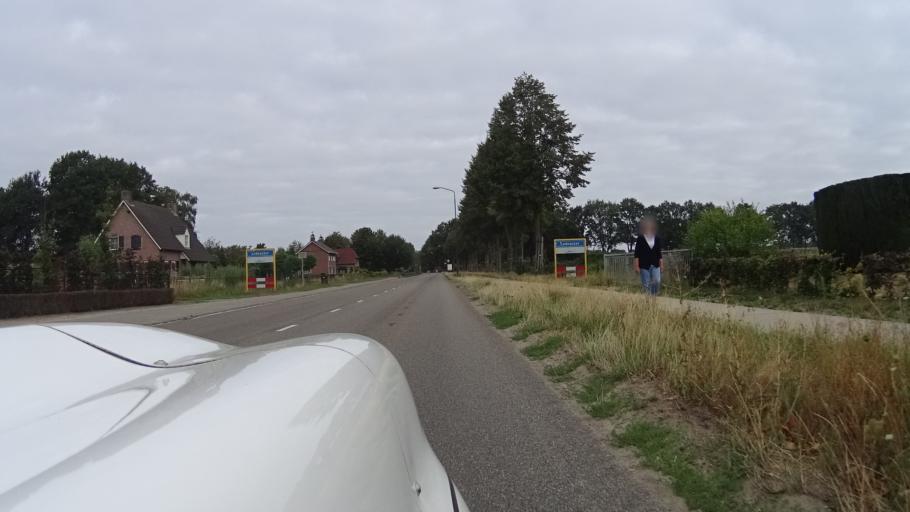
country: NL
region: North Brabant
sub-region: Gemeente Sint Anthonis
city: Sint Anthonis
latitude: 51.6314
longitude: 5.8778
